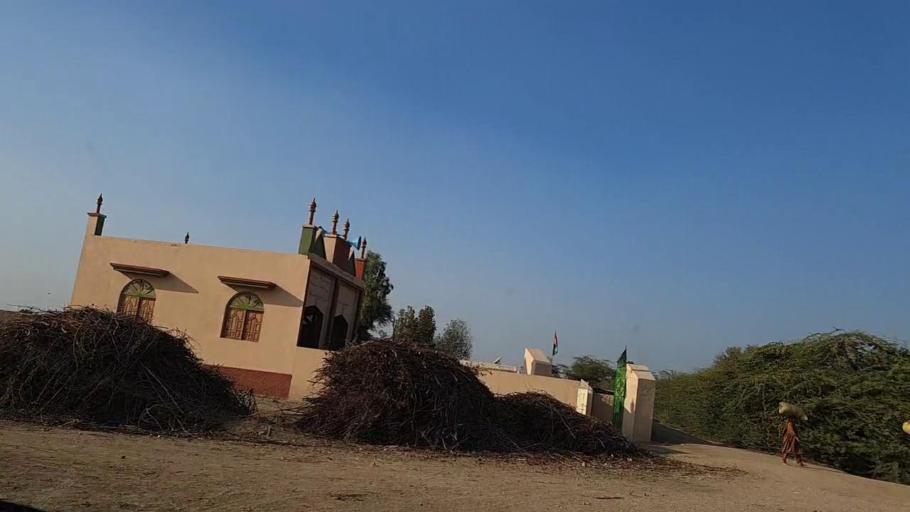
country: PK
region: Sindh
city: Sakrand
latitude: 26.0928
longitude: 68.2069
